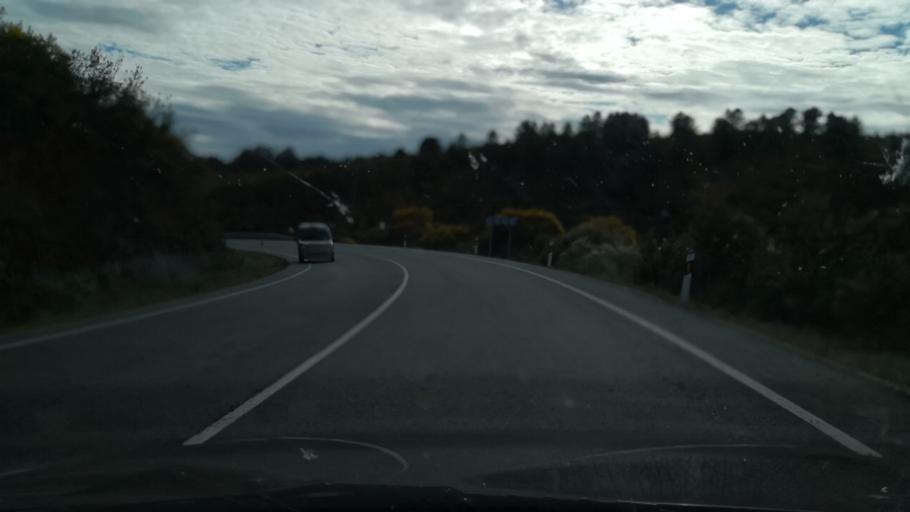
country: ES
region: Extremadura
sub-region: Provincia de Caceres
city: Perales del Puerto
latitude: 40.1276
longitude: -6.6793
